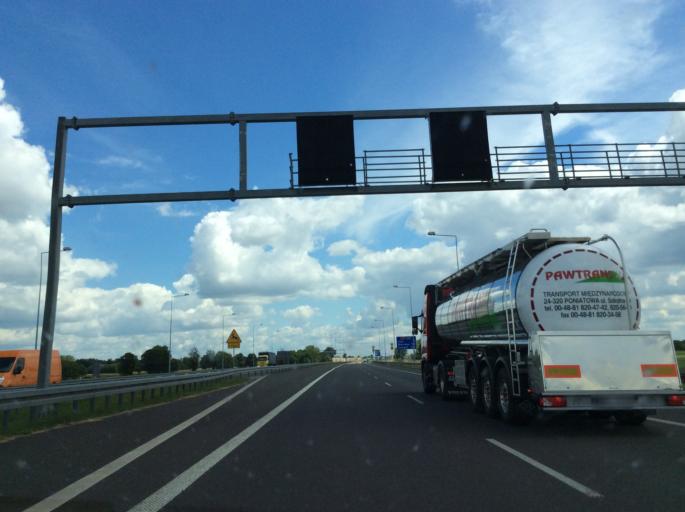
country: PL
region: Greater Poland Voivodeship
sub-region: Powiat turecki
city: Brudzew
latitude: 52.1391
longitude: 18.6168
